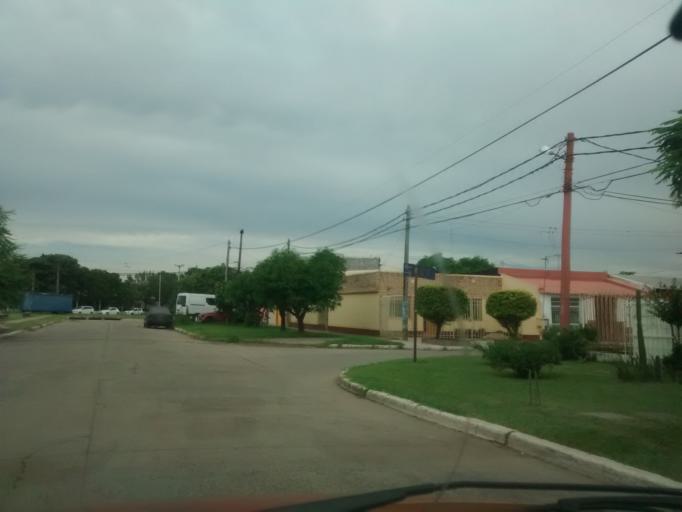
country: AR
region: Chaco
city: Resistencia
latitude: -27.4555
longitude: -59.0157
